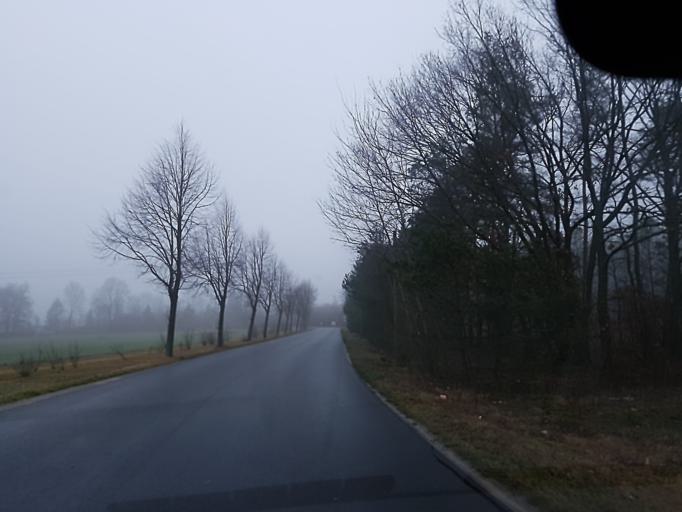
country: DE
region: Brandenburg
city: Finsterwalde
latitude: 51.6381
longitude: 13.7396
